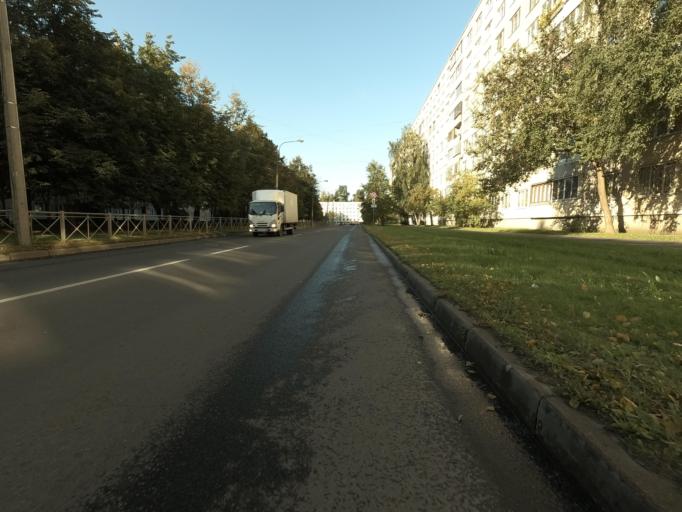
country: RU
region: St.-Petersburg
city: Kolpino
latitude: 59.7401
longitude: 30.5691
